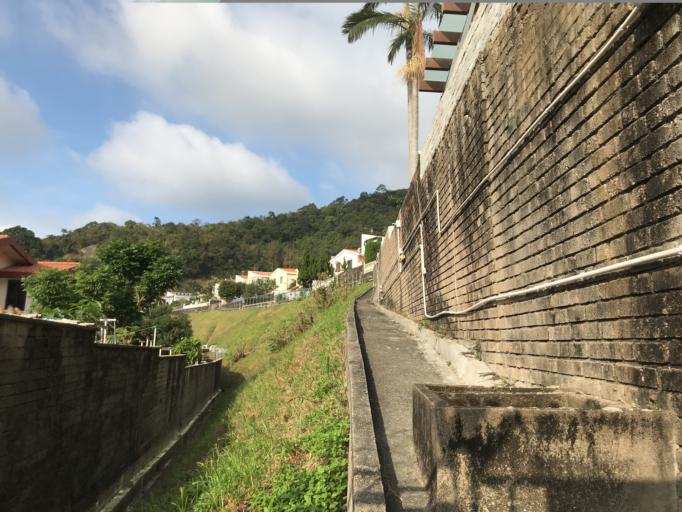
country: HK
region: Tai Po
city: Tai Po
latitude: 22.4630
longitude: 114.1606
